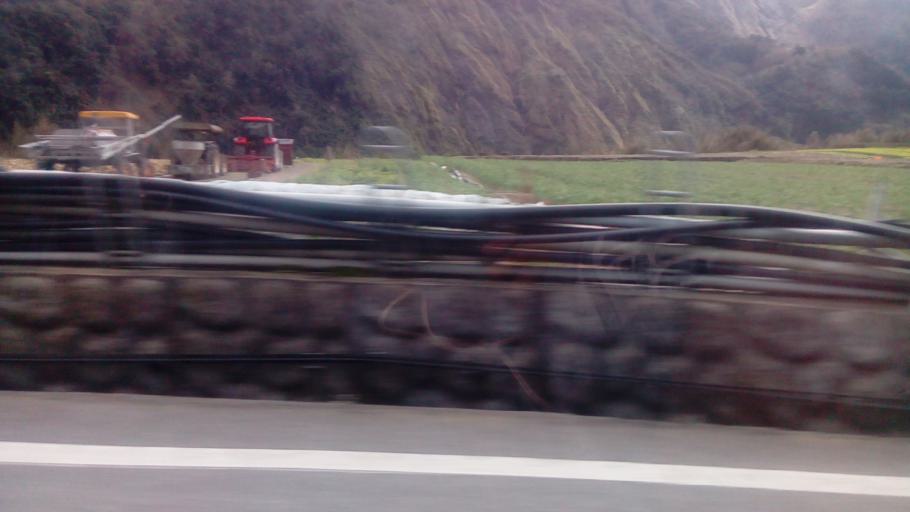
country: TW
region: Taiwan
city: Daxi
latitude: 24.4689
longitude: 121.4068
